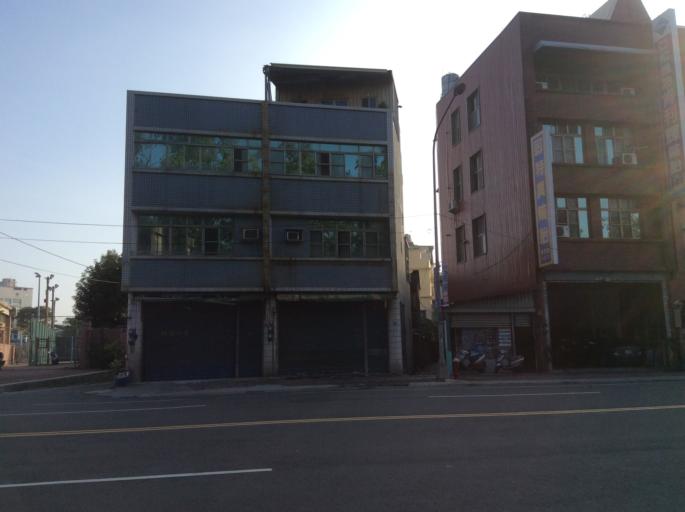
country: TW
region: Kaohsiung
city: Kaohsiung
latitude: 22.6937
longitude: 120.2939
